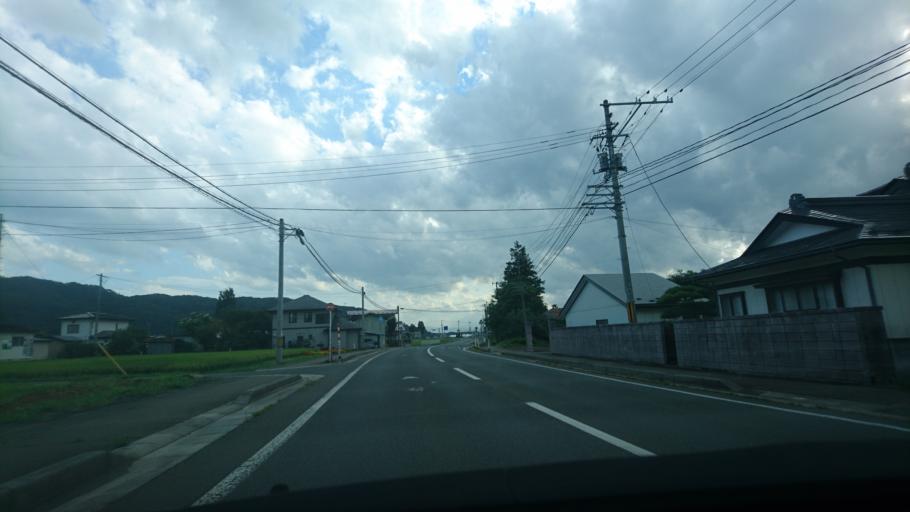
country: JP
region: Iwate
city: Kitakami
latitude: 39.2868
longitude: 141.1391
